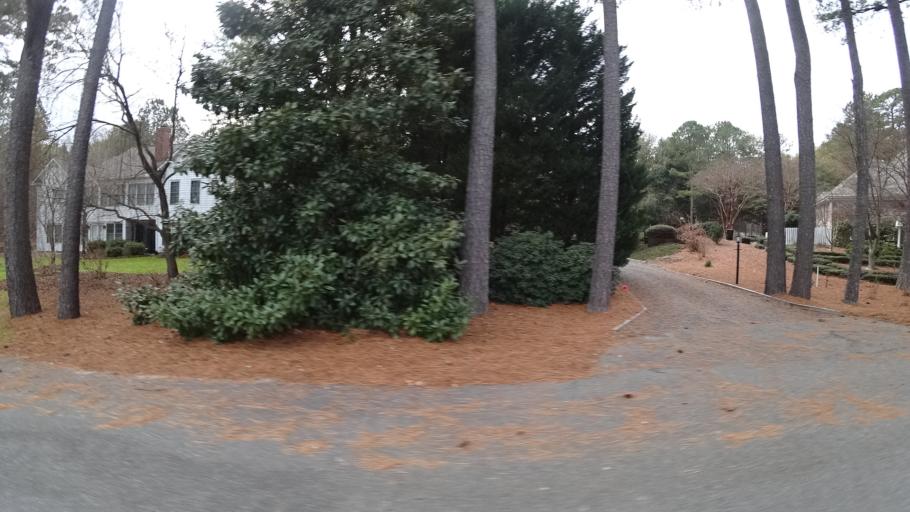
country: US
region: North Carolina
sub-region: Moore County
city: Pinehurst
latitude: 35.1998
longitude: -79.4721
